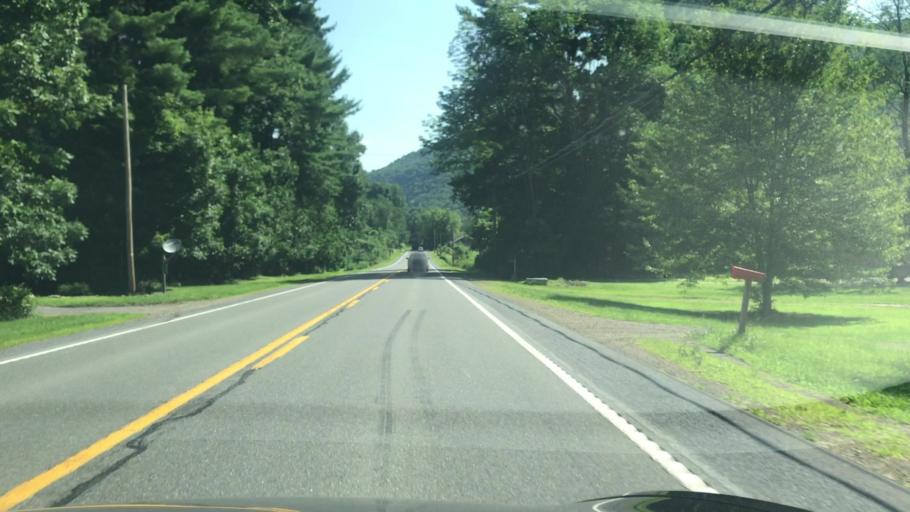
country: US
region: Pennsylvania
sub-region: Bradford County
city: Canton
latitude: 41.4873
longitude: -76.9719
